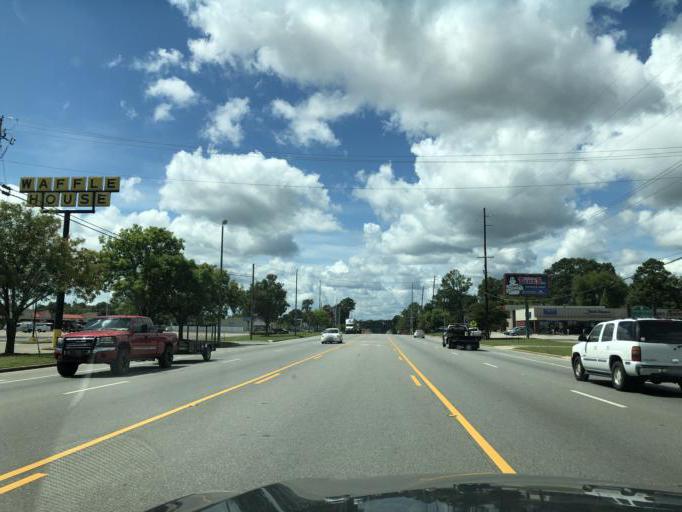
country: US
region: Alabama
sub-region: Barbour County
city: Eufaula
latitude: 31.8737
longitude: -85.1536
